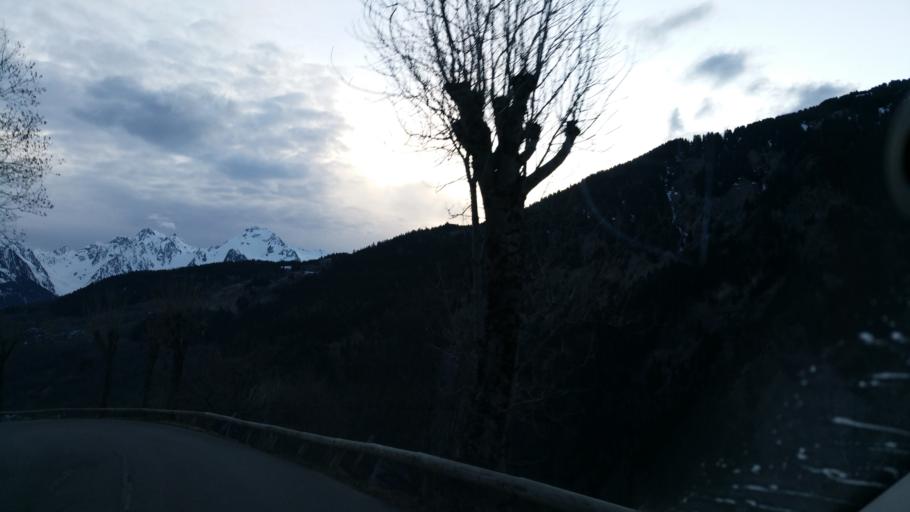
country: FR
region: Rhone-Alpes
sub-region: Departement de la Savoie
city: La Chambre
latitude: 45.4020
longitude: 6.3401
